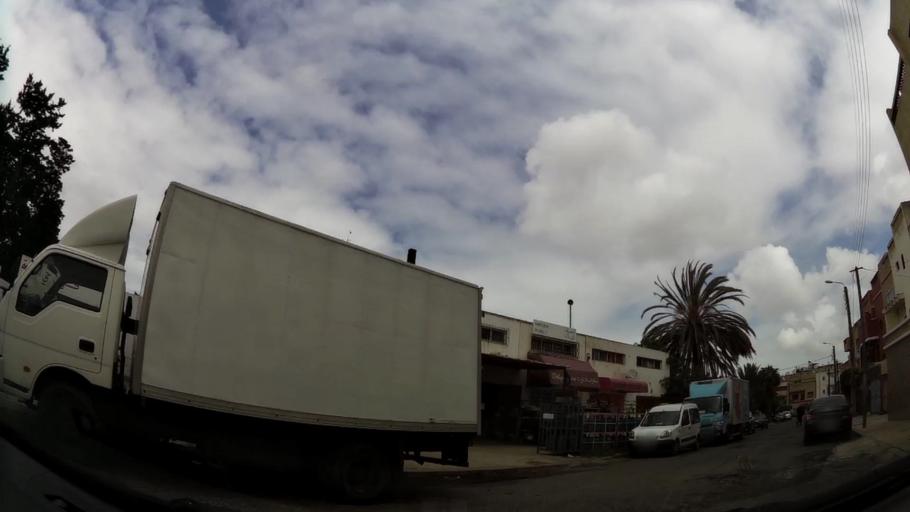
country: MA
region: Grand Casablanca
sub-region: Casablanca
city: Casablanca
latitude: 33.5364
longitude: -7.5992
